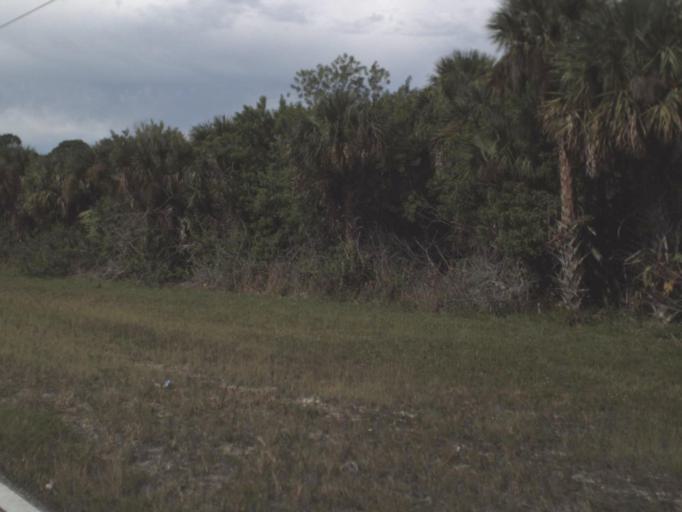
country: US
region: Florida
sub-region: Brevard County
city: Merritt Island
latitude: 28.5265
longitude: -80.7202
